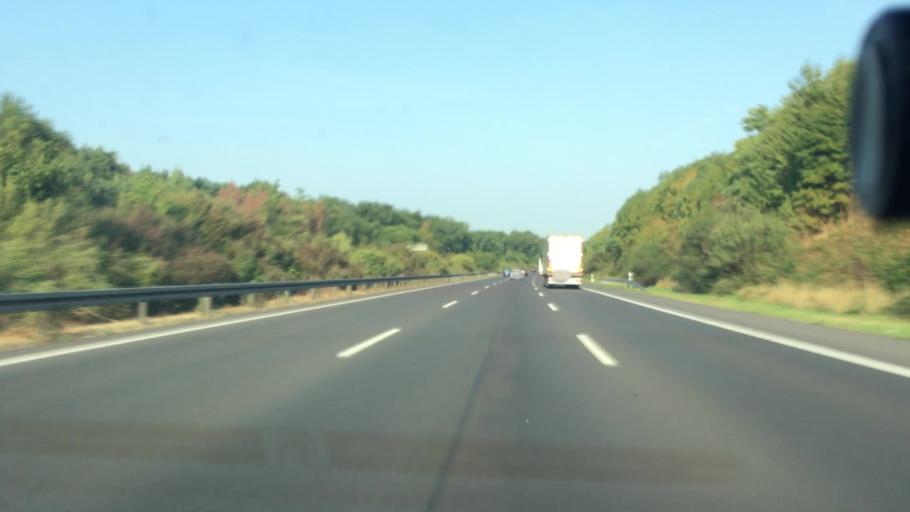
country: DE
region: Lower Saxony
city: Rennau
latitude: 52.2828
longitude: 10.9108
